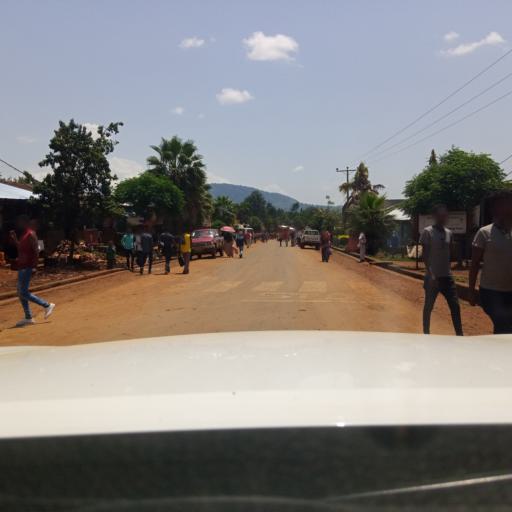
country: ET
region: Oromiya
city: Agaro
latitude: 8.0906
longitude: 36.9506
